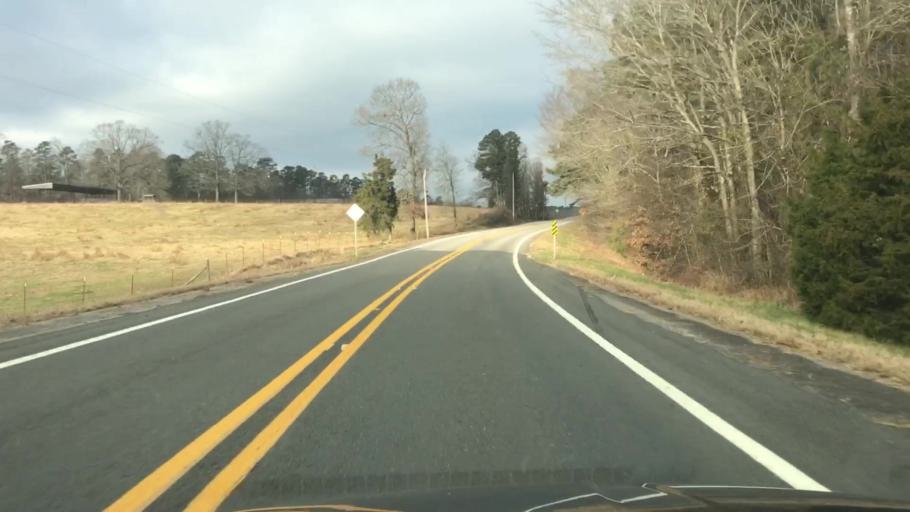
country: US
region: Arkansas
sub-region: Montgomery County
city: Mount Ida
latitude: 34.6598
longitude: -93.7656
